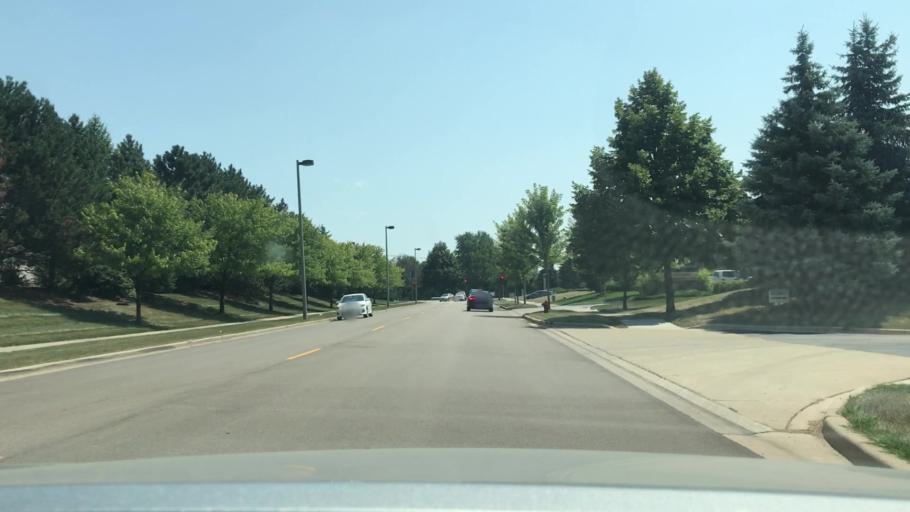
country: US
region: Illinois
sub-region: Kane County
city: Aurora
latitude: 41.7339
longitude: -88.2304
